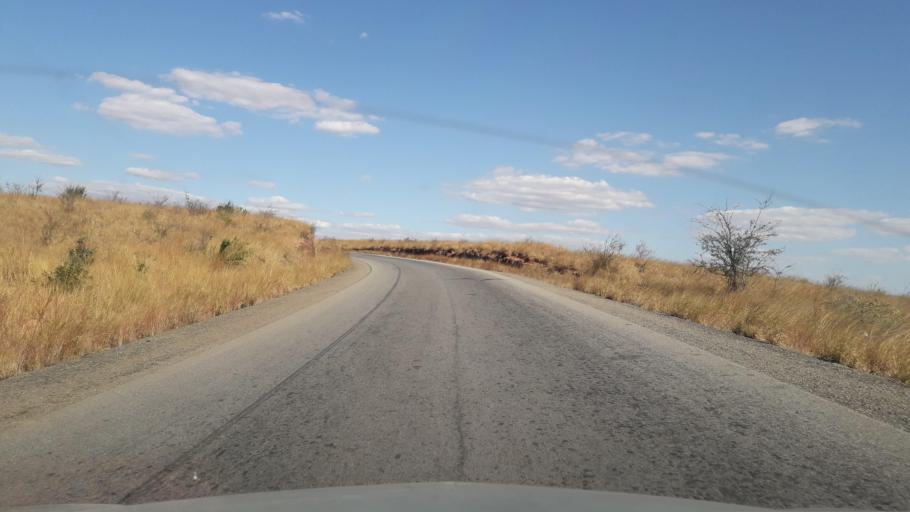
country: MG
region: Betsiboka
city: Maevatanana
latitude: -17.1591
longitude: 46.8393
